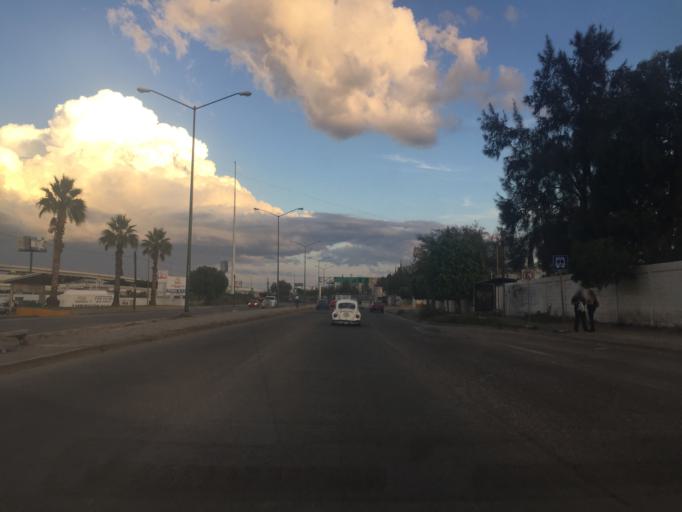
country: MX
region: Guanajuato
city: Leon
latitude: 21.0959
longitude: -101.6312
